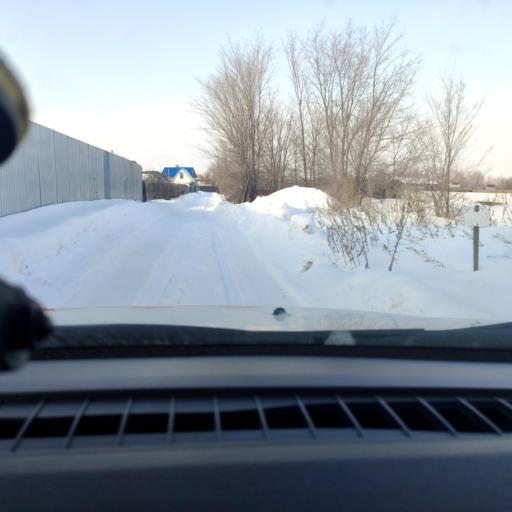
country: RU
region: Samara
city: Samara
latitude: 53.1301
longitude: 50.2594
